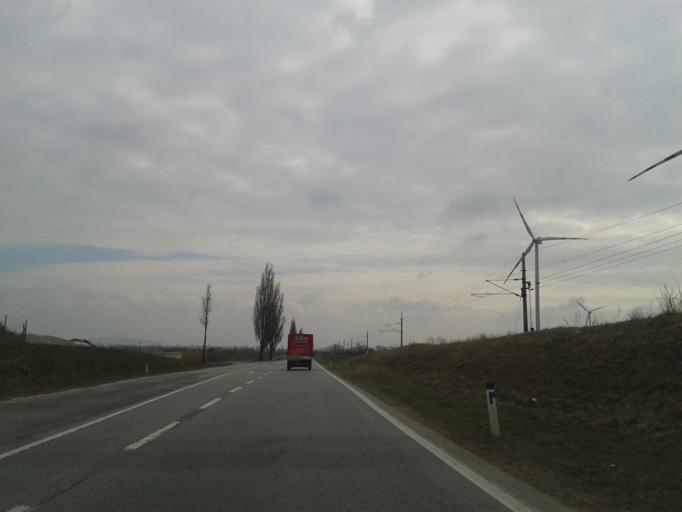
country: AT
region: Lower Austria
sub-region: Politischer Bezirk Ganserndorf
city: Orth an der Donau
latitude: 48.1085
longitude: 16.7367
